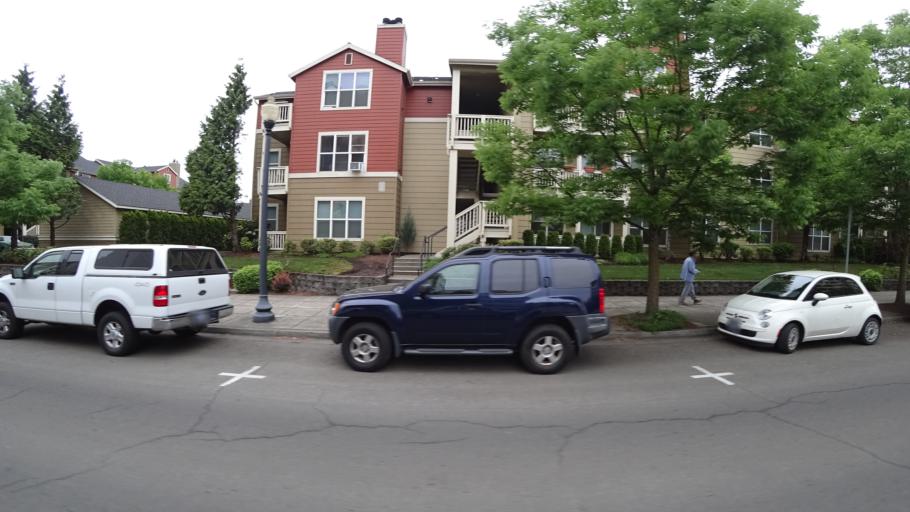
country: US
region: Oregon
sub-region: Washington County
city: Rockcreek
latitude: 45.5398
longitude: -122.8778
